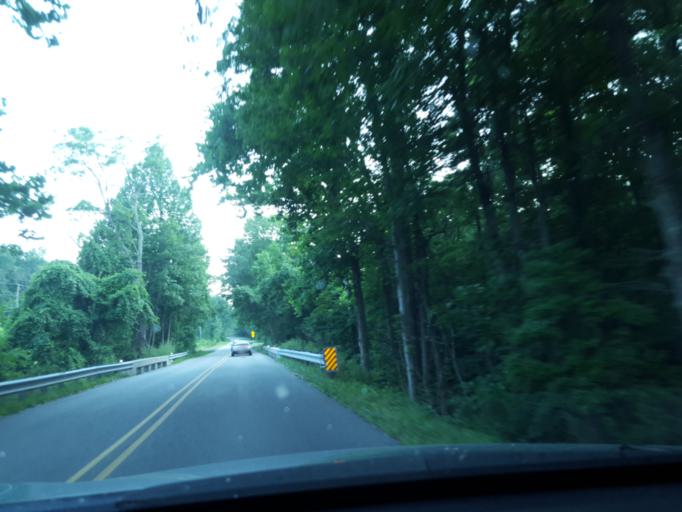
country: US
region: Virginia
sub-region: Augusta County
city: Lyndhurst
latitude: 37.9409
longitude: -78.9678
